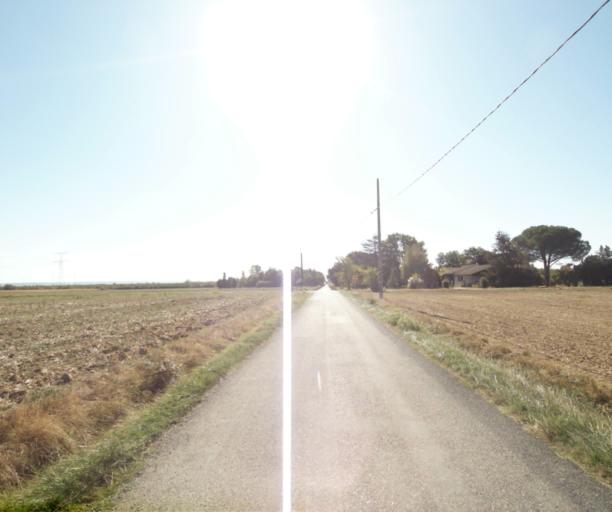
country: FR
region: Midi-Pyrenees
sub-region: Departement du Tarn-et-Garonne
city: Verdun-sur-Garonne
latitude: 43.8352
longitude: 1.2194
